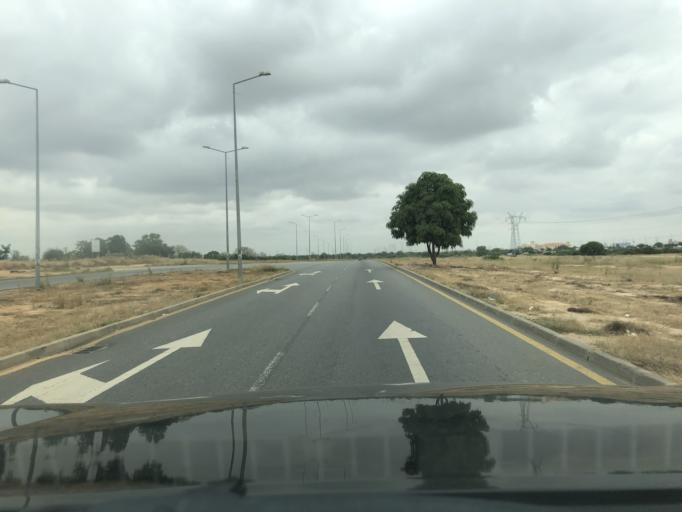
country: AO
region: Luanda
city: Luanda
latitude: -8.9757
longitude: 13.2815
